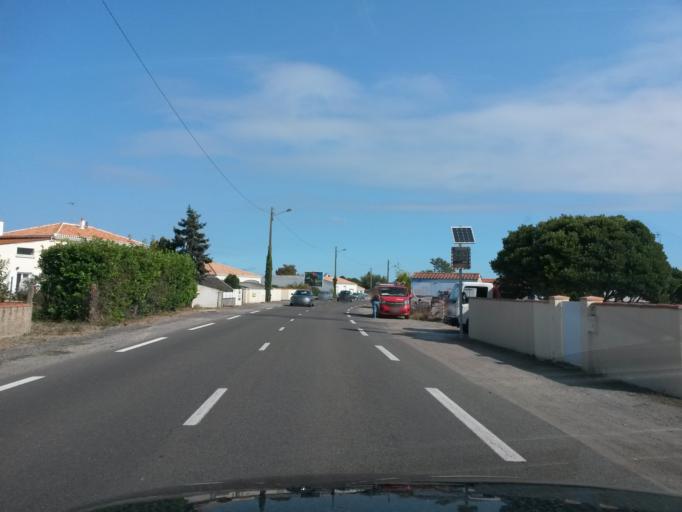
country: FR
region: Pays de la Loire
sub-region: Departement de la Vendee
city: Olonne-sur-Mer
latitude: 46.5541
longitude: -1.8095
